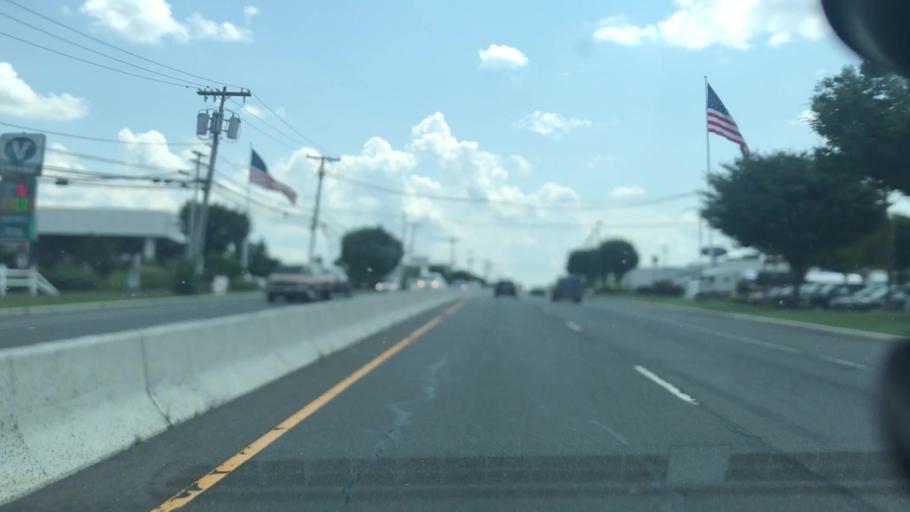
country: US
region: New Jersey
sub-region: Hunterdon County
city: Flemington
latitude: 40.4890
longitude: -74.8625
